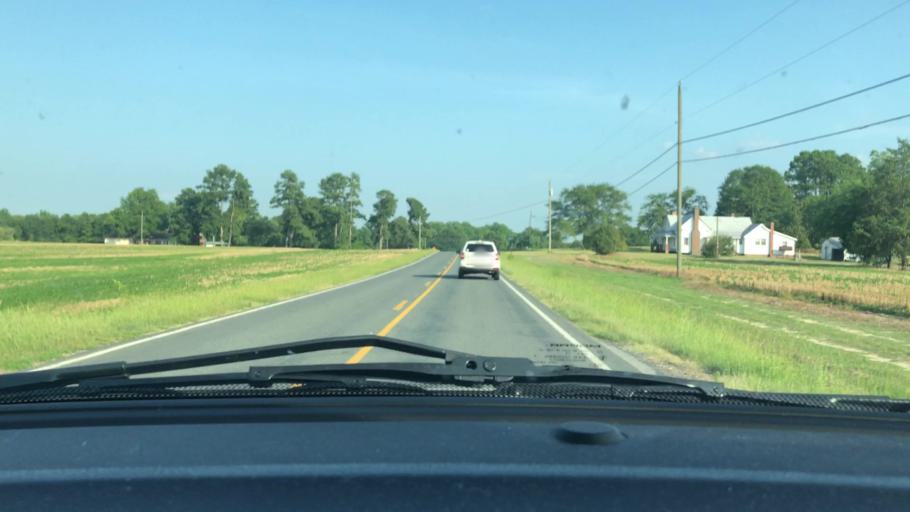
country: US
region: North Carolina
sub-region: Lee County
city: Broadway
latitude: 35.3656
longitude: -79.0933
